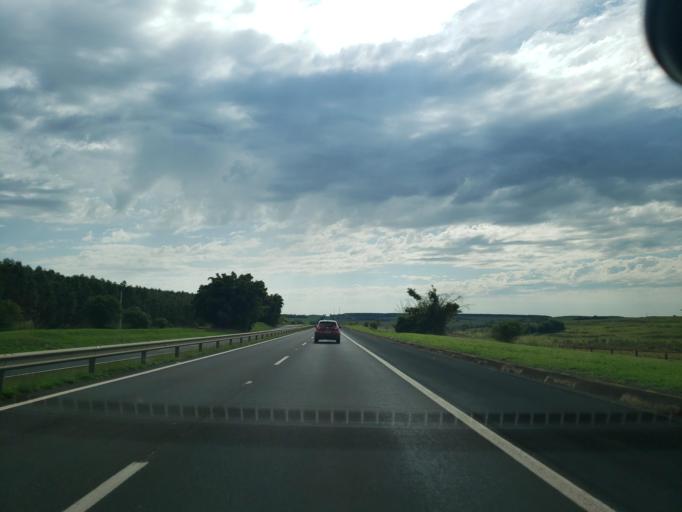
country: BR
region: Sao Paulo
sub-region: Cafelandia
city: Cafelandia
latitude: -21.7914
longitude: -49.6500
